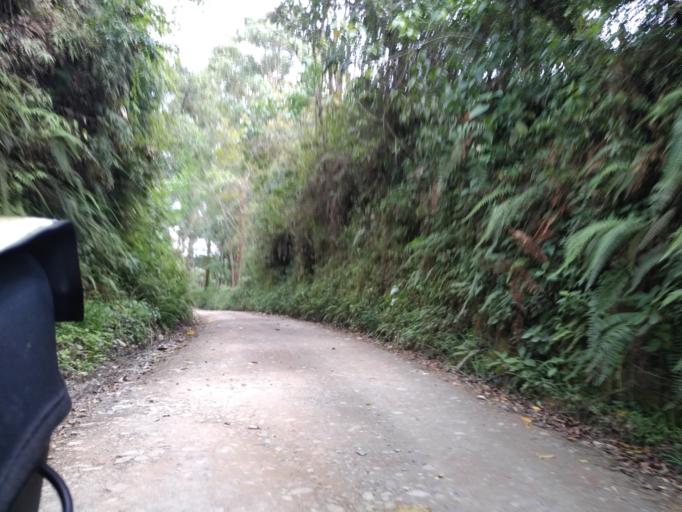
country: CO
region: Quindio
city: Salento
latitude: 4.6316
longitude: -75.5814
